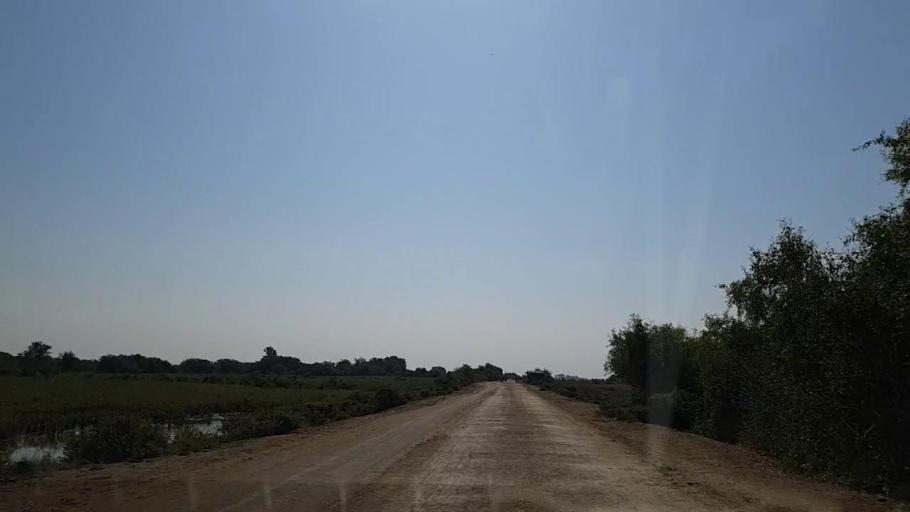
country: PK
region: Sindh
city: Chuhar Jamali
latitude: 24.5173
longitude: 68.0947
